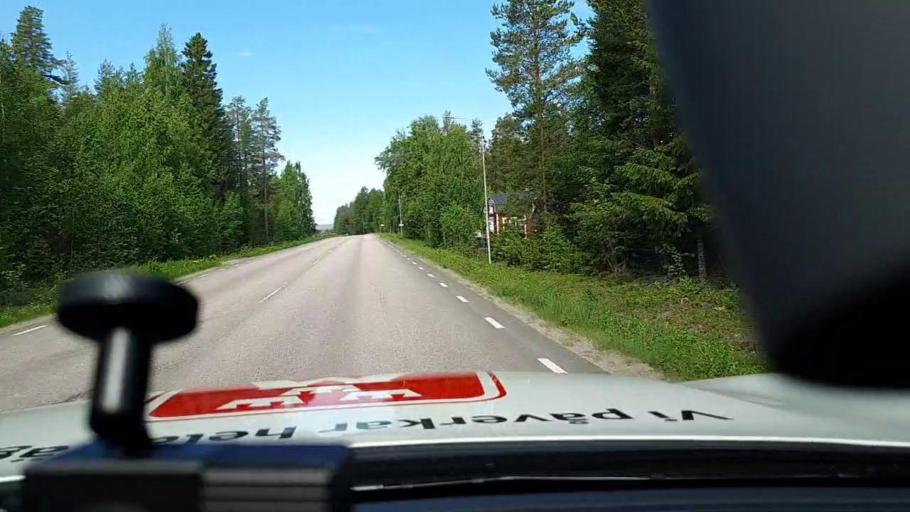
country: SE
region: Norrbotten
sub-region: Lulea Kommun
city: Sodra Sunderbyn
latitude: 65.6468
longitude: 21.8815
